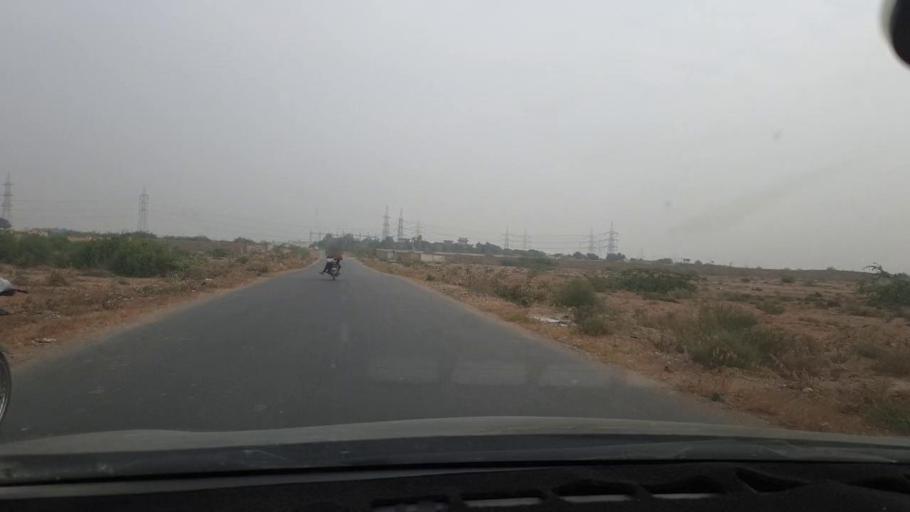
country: PK
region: Sindh
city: Malir Cantonment
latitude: 24.9128
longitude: 67.2762
